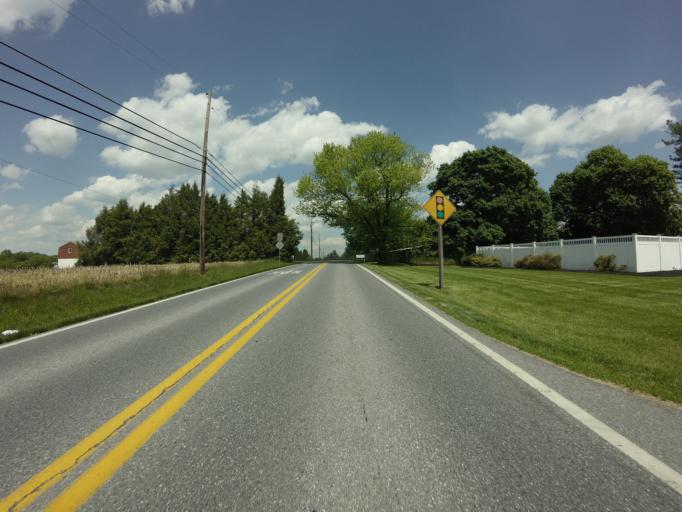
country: US
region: Maryland
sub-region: Carroll County
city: Mount Airy
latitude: 39.3488
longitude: -77.1838
